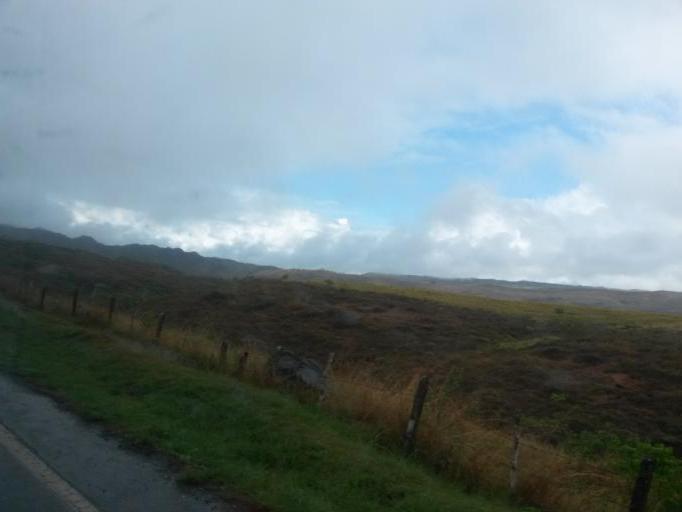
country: CO
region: Cauca
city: El Bordo
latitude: 2.1502
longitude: -76.9185
